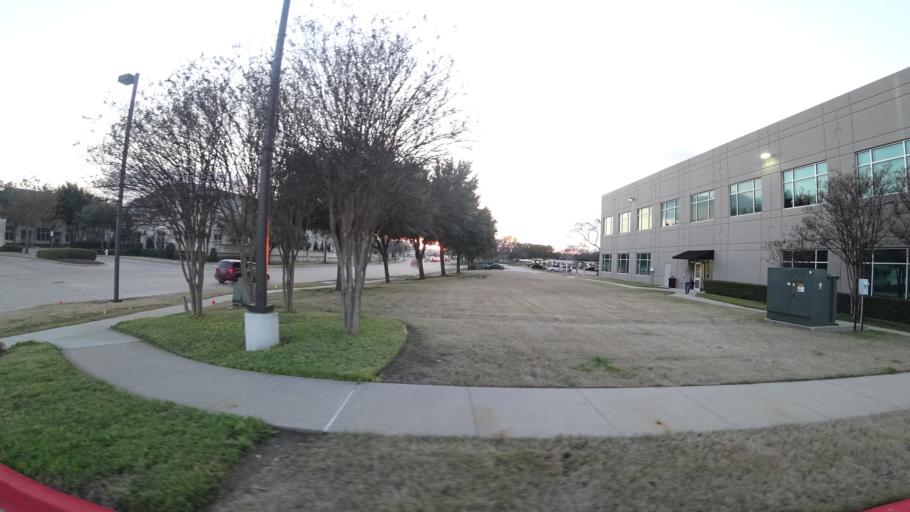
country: US
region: Texas
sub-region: Dallas County
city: Coppell
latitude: 32.9913
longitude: -96.9718
